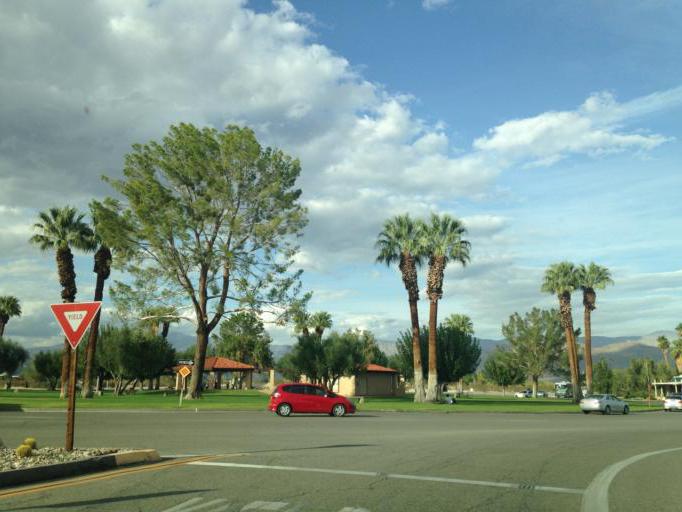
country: US
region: California
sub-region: San Diego County
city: Borrego Springs
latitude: 33.2557
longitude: -116.3750
